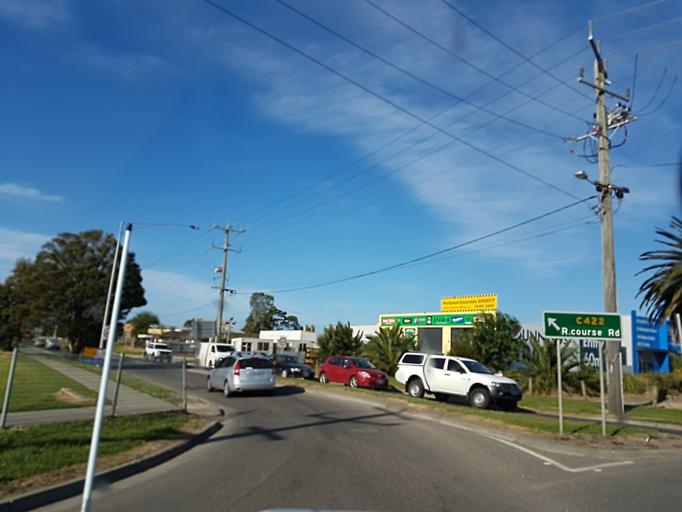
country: AU
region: Victoria
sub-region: Cardinia
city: Pakenham South
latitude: -38.0837
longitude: 145.4919
